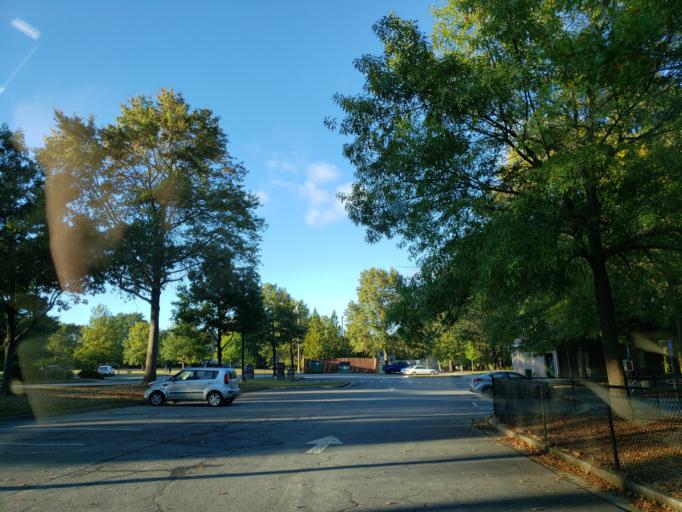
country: US
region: Georgia
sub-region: Cobb County
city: Marietta
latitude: 33.9482
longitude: -84.5723
